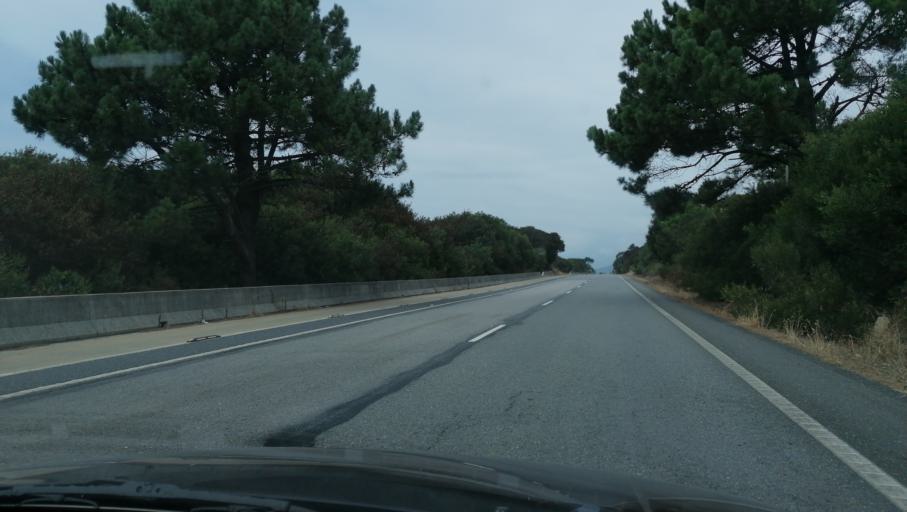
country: ES
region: Galicia
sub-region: Provincia de Pontevedra
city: Oia
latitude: 41.9805
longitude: -8.8846
